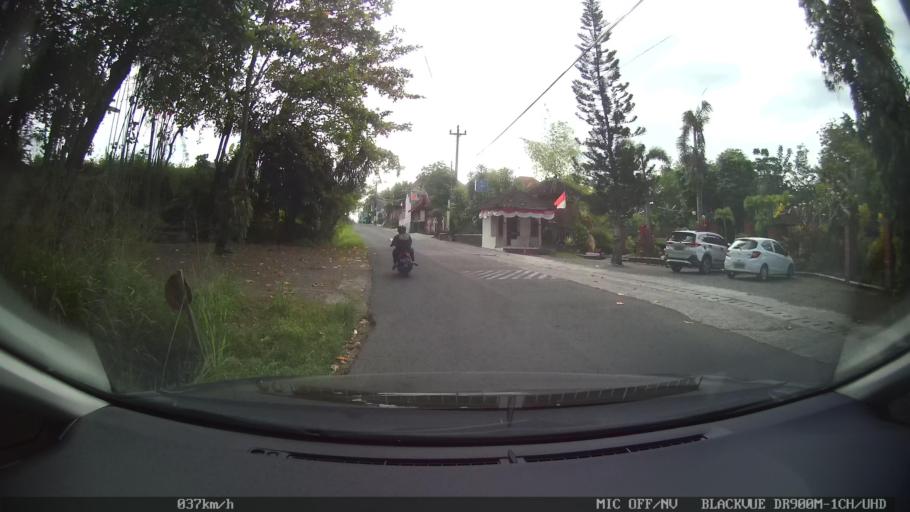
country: ID
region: Daerah Istimewa Yogyakarta
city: Depok
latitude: -7.7358
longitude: 110.4153
